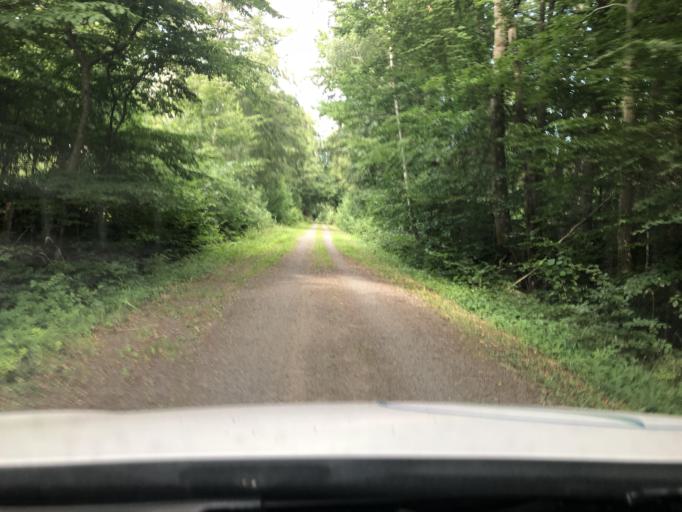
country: SE
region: Skane
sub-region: Kristianstads Kommun
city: Degeberga
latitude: 55.7796
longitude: 14.1708
